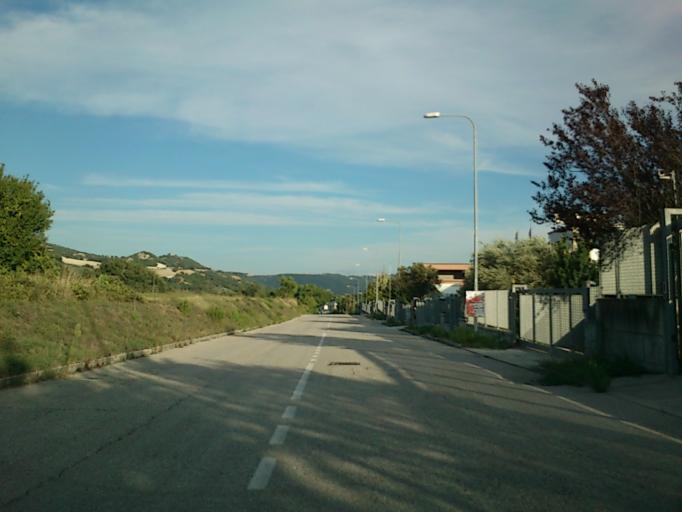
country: IT
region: The Marches
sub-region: Provincia di Pesaro e Urbino
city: Canavaccio
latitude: 43.6916
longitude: 12.6999
